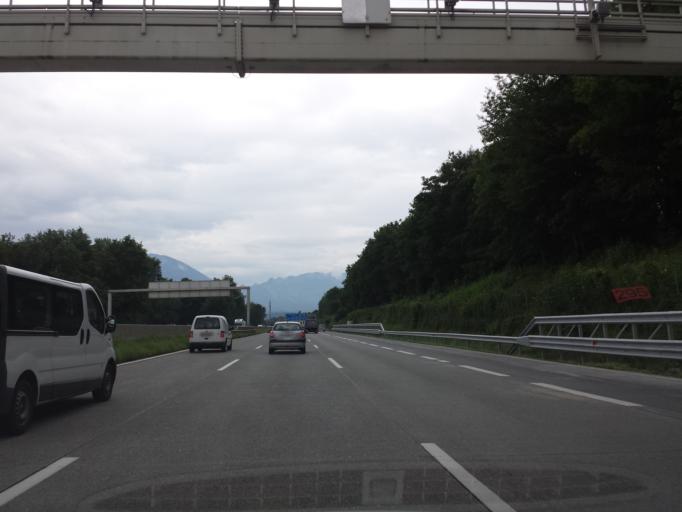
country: DE
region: Bavaria
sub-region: Upper Bavaria
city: Freilassing
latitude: 47.8017
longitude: 12.9895
